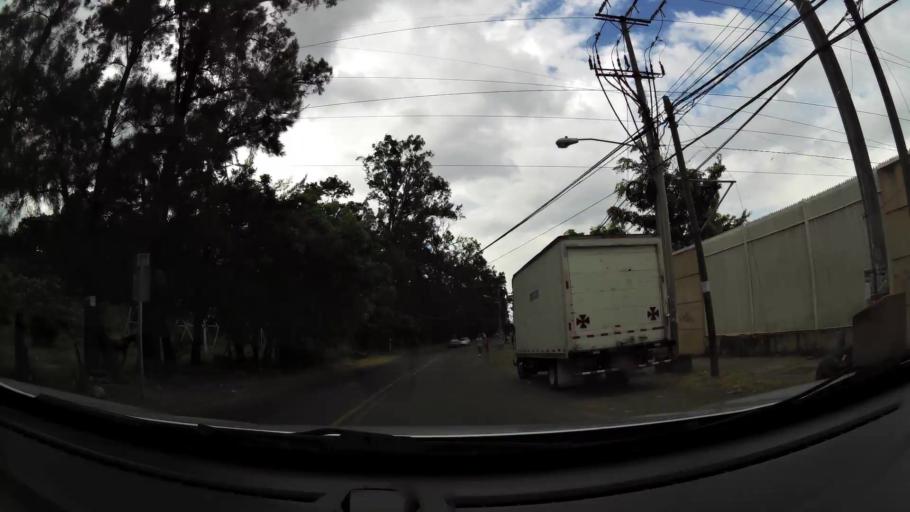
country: CR
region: San Jose
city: San Felipe
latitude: 9.9121
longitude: -84.1110
